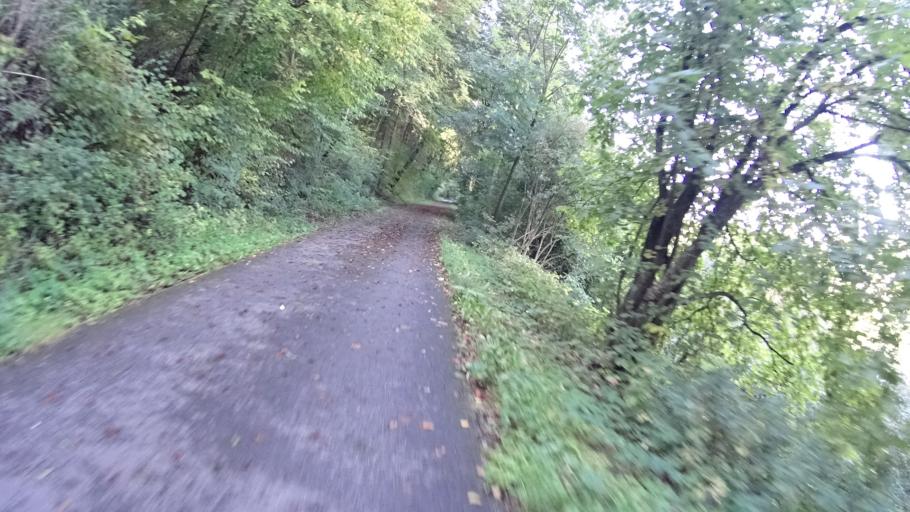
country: DE
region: Bavaria
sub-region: Upper Bavaria
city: Eichstaett
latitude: 48.8741
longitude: 11.2298
